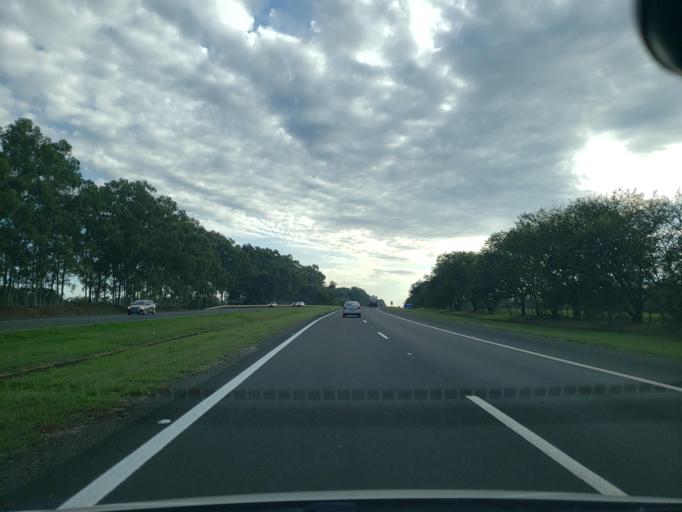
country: BR
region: Sao Paulo
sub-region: Guararapes
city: Guararapes
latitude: -21.2149
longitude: -50.6910
